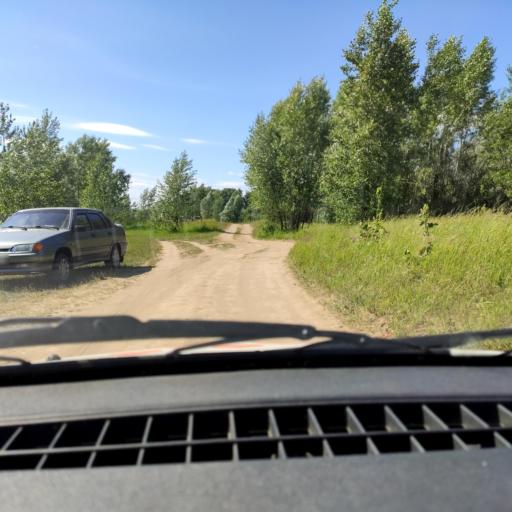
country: RU
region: Bashkortostan
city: Iglino
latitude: 54.8001
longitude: 56.2252
